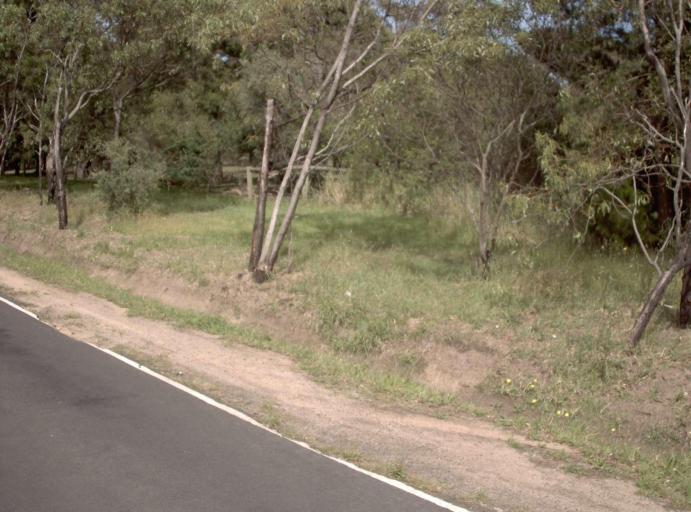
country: AU
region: Victoria
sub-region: Bass Coast
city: Phillip Island
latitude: -38.4688
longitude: 145.1914
